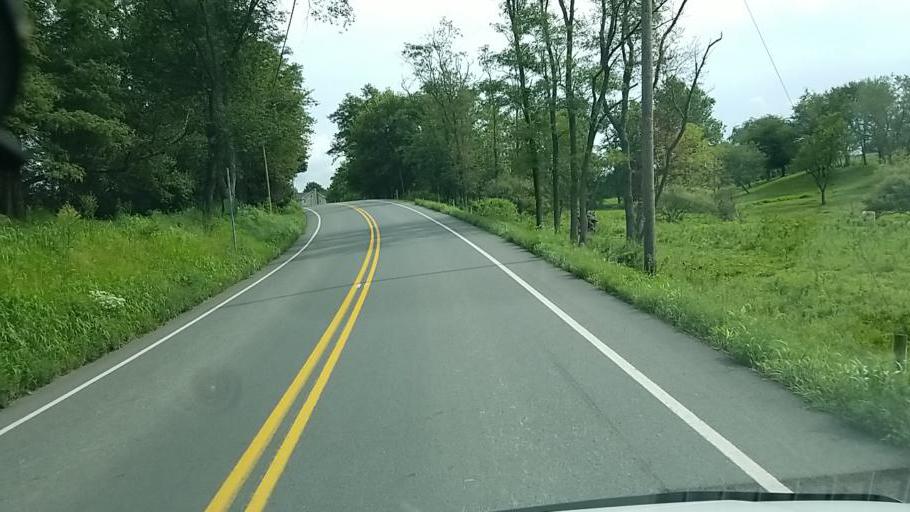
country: US
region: Pennsylvania
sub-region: Dauphin County
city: Elizabethville
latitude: 40.6135
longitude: -76.7831
